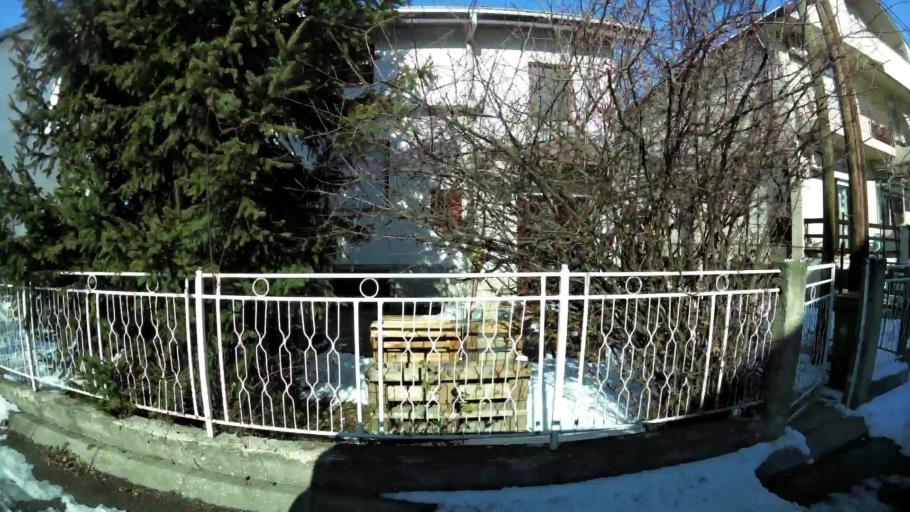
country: MK
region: Saraj
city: Saraj
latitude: 42.0080
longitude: 21.3490
